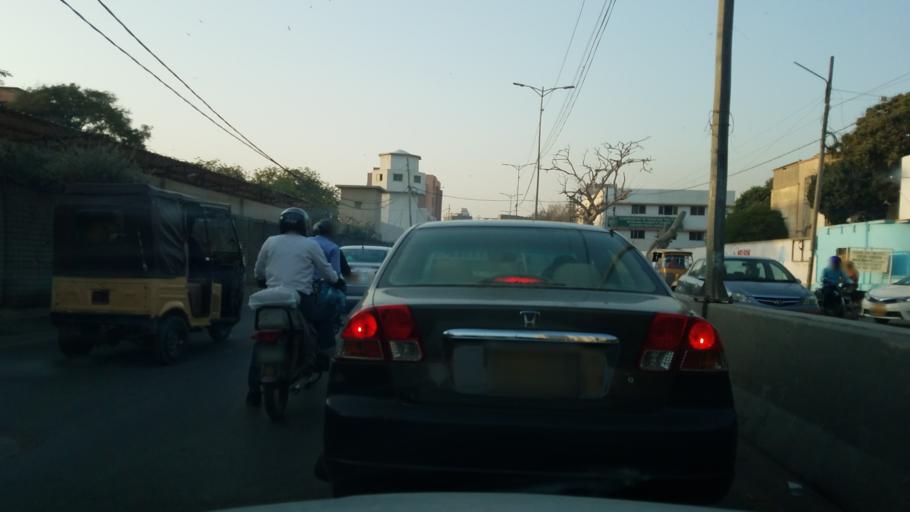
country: PK
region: Sindh
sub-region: Karachi District
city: Karachi
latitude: 24.8698
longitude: 67.0220
